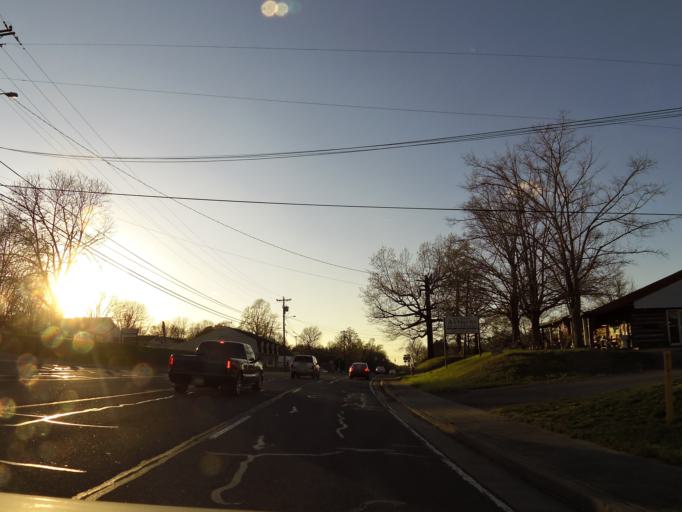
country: US
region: Tennessee
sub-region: Robertson County
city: Ridgetop
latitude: 36.3974
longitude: -86.7705
